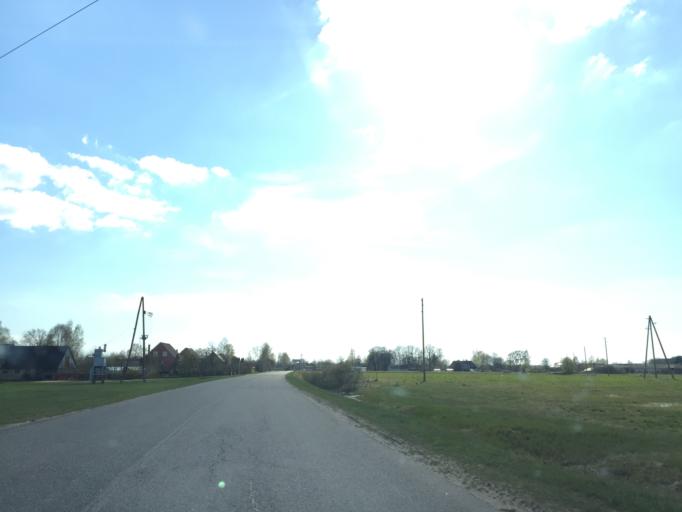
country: LV
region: Saulkrastu
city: Saulkrasti
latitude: 57.3340
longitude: 24.5003
